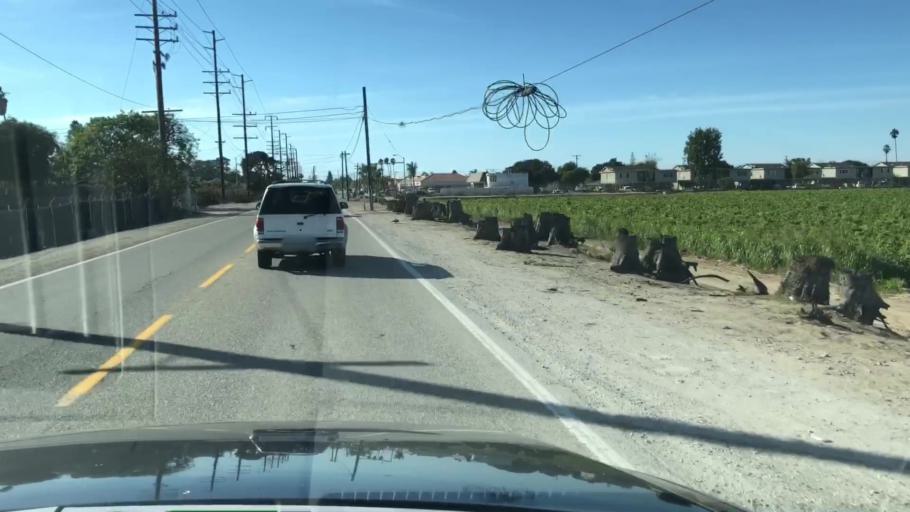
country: US
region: California
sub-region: Ventura County
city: Oxnard
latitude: 34.1732
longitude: -119.1465
